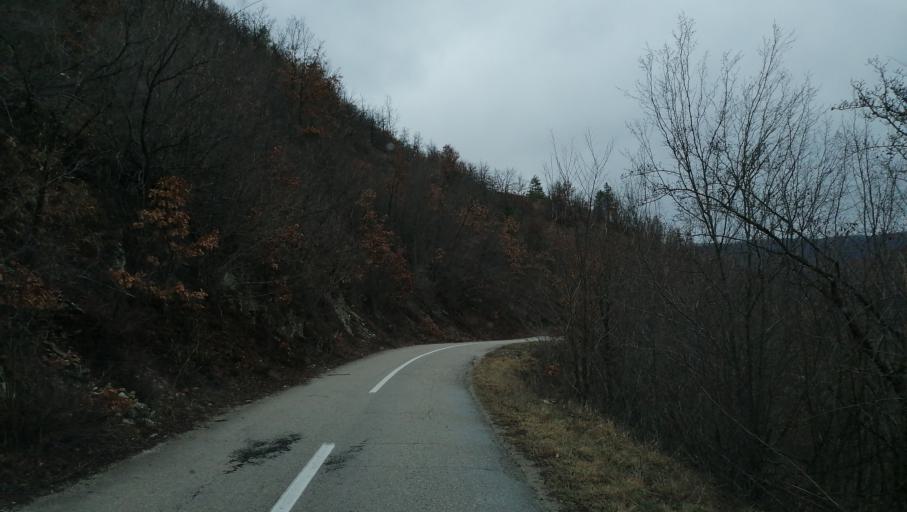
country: RS
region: Central Serbia
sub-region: Pirotski Okrug
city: Dimitrovgrad
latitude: 42.9554
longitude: 22.7802
